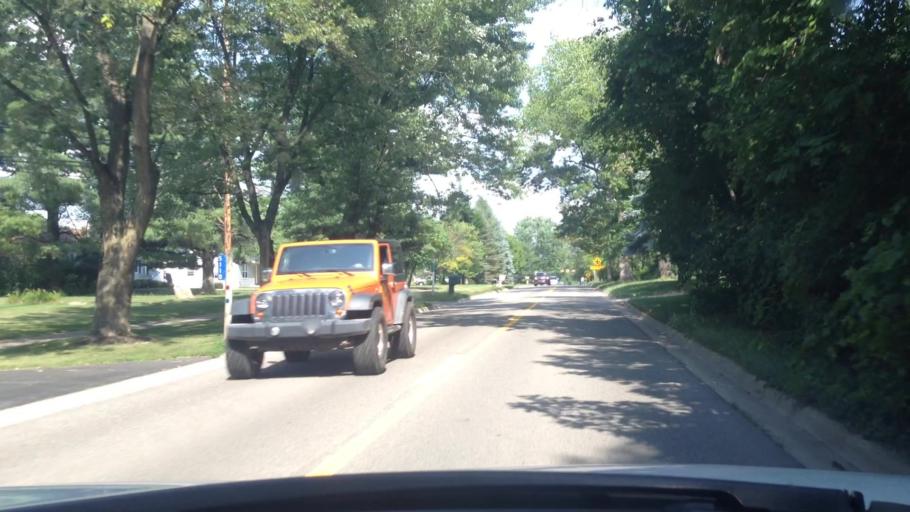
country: US
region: Michigan
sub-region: Oakland County
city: Clarkston
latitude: 42.7344
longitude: -83.3542
